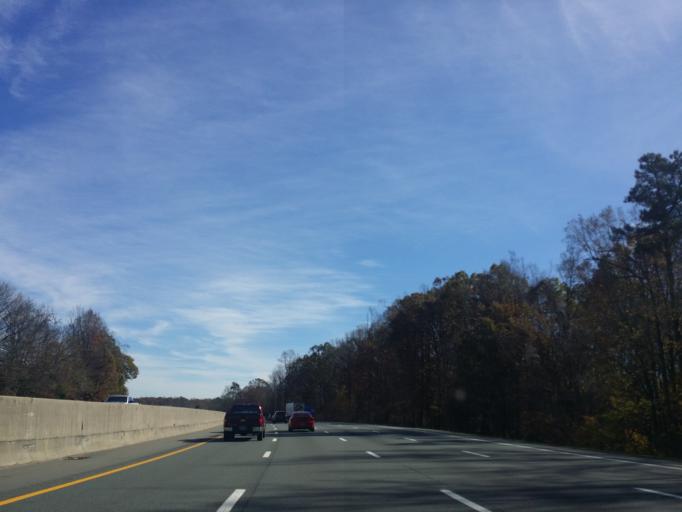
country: US
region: North Carolina
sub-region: Alamance County
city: Haw River
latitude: 36.0657
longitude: -79.3219
